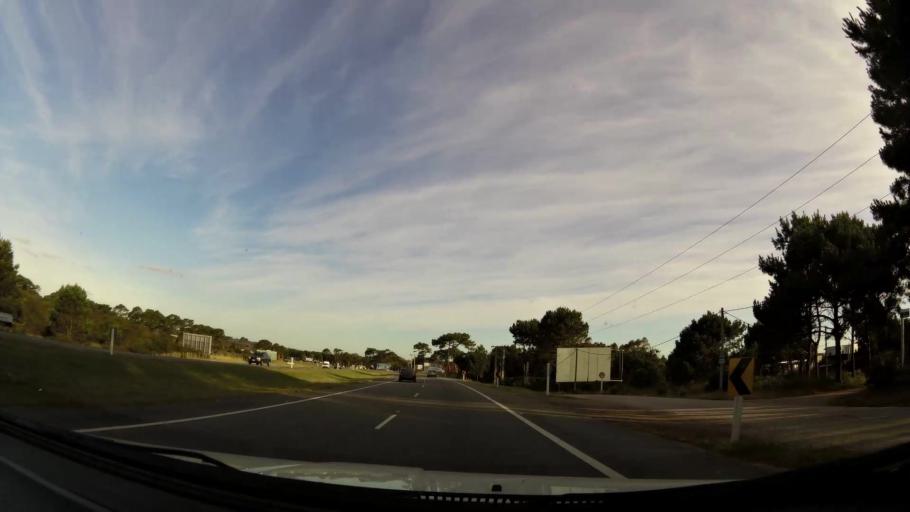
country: UY
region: Maldonado
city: Maldonado
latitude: -34.8723
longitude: -55.0778
